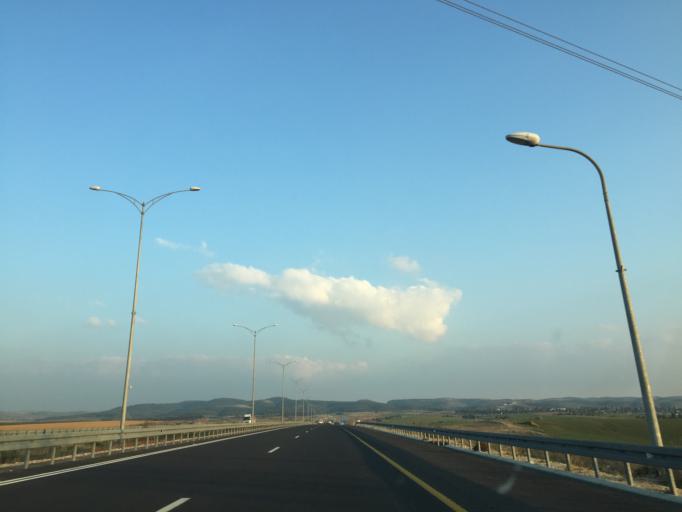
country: IL
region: Southern District
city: Lehavim
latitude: 31.3900
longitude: 34.7969
